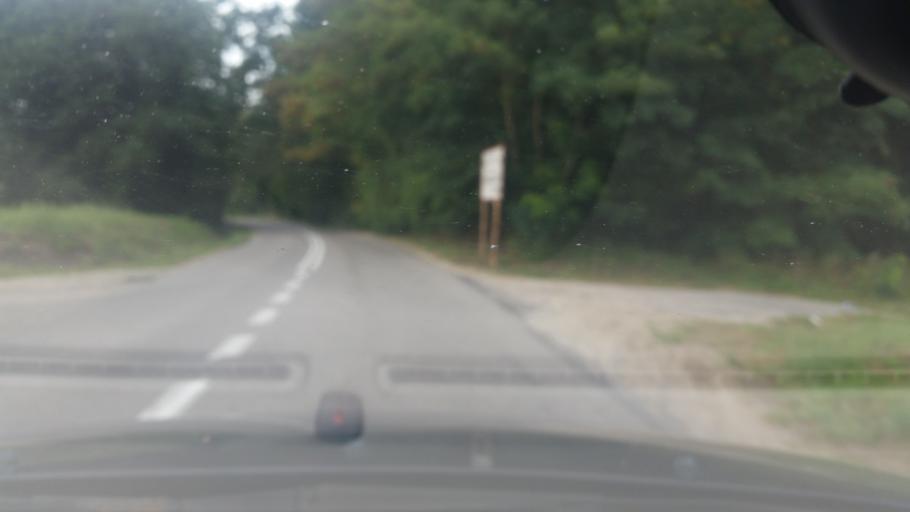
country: PL
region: Pomeranian Voivodeship
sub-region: Powiat leborski
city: Leba
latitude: 54.7408
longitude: 17.6438
